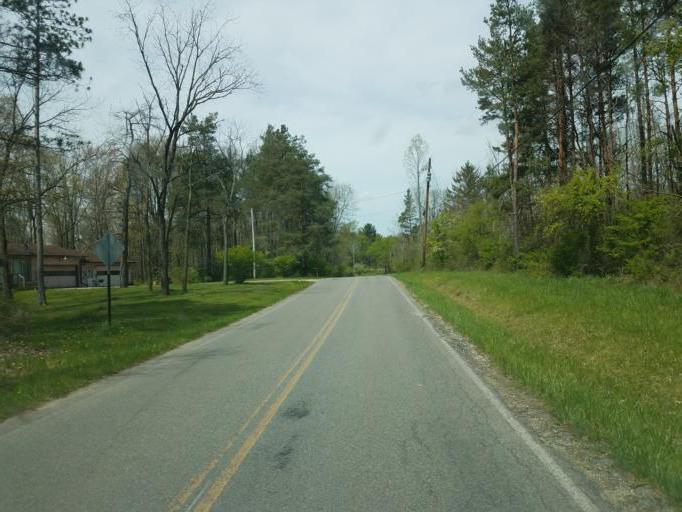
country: US
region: Ohio
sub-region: Summit County
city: Peninsula
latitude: 41.2157
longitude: -81.5815
